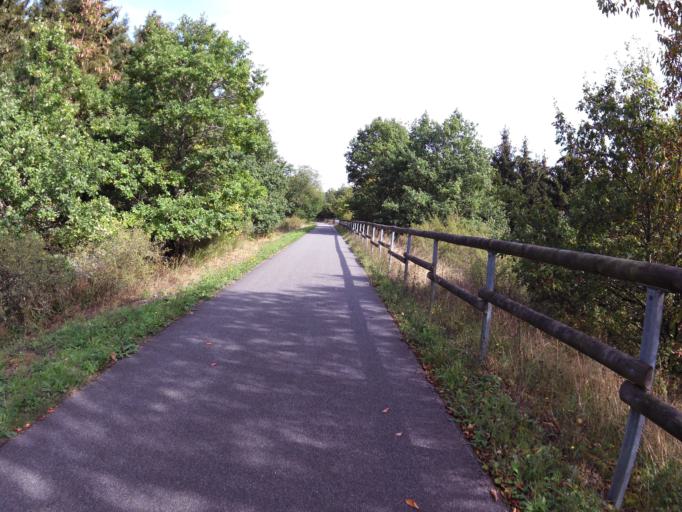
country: DE
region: Rheinland-Pfalz
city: Lunebach
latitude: 50.1410
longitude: 6.3339
